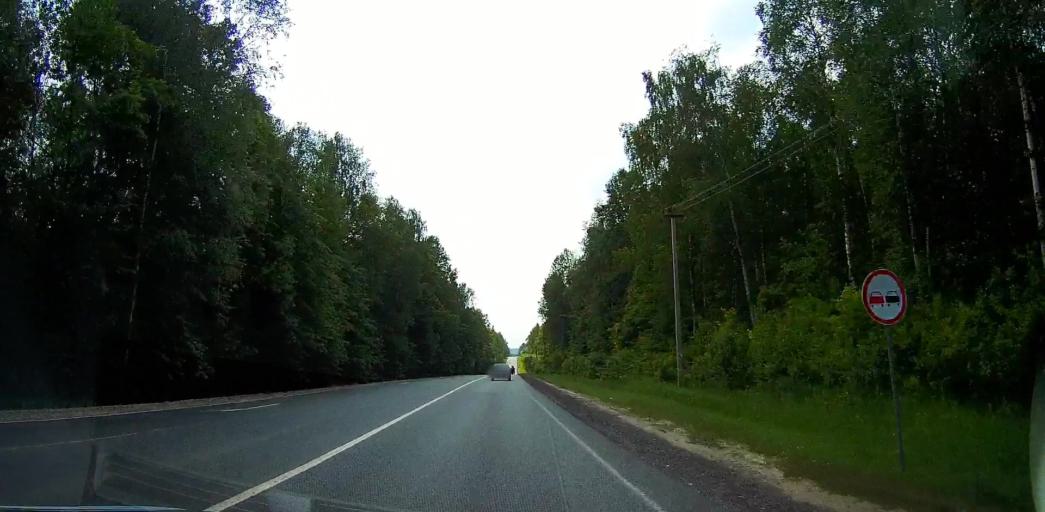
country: RU
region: Moskovskaya
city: Stupino
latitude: 54.9801
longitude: 38.1653
